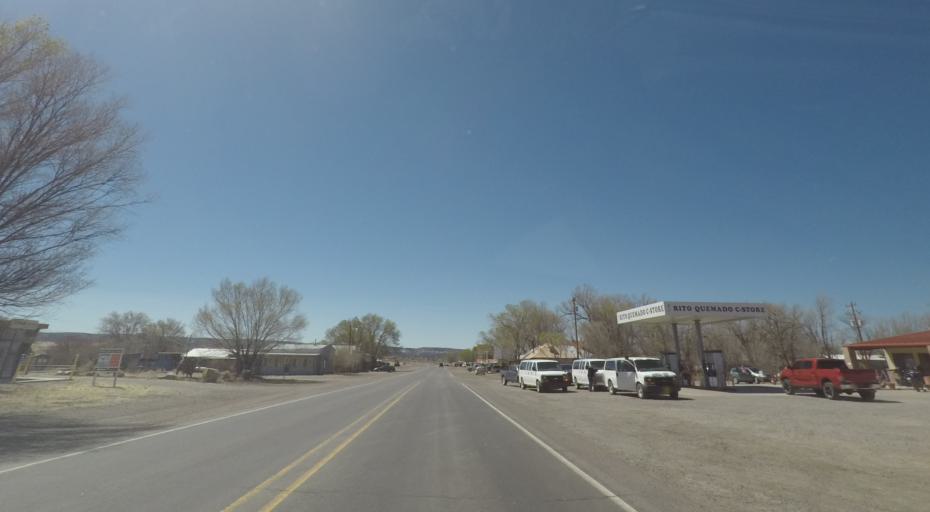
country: US
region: New Mexico
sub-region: Catron County
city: Reserve
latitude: 34.3432
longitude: -108.4965
